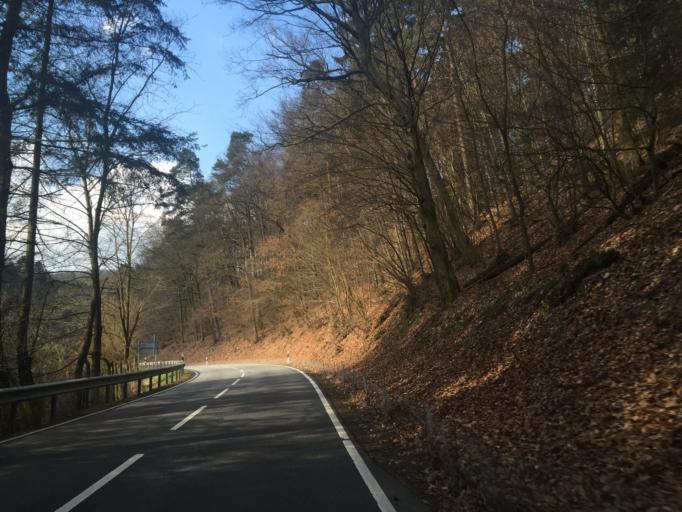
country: DE
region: Baden-Wuerttemberg
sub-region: Karlsruhe Region
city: Wilhelmsfeld
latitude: 49.4834
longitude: 8.7268
